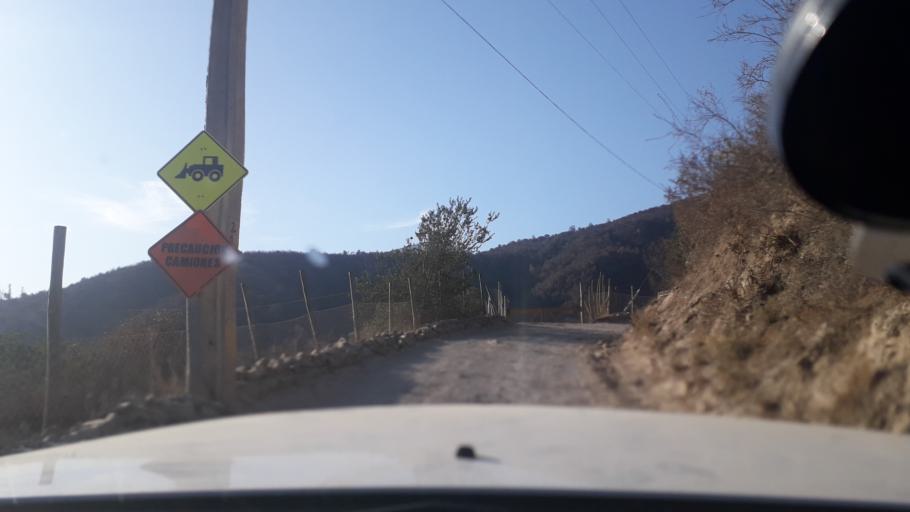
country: CL
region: Valparaiso
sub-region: Provincia de Marga Marga
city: Limache
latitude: -33.0533
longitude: -71.0893
